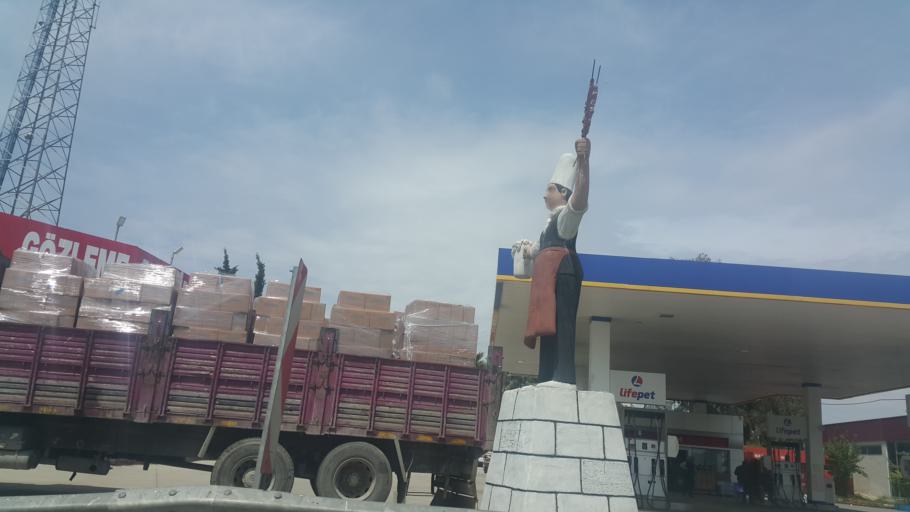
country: TR
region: Adana
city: Yakapinar
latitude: 36.9656
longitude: 35.6104
